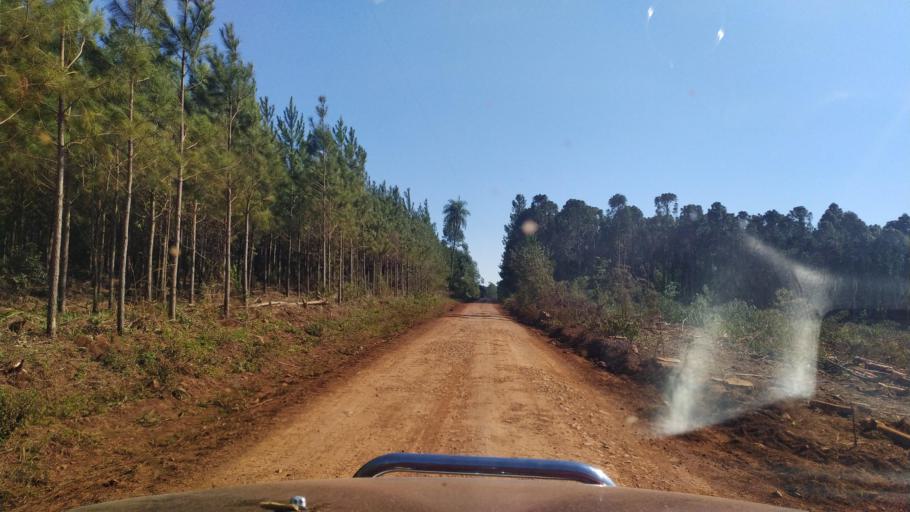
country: AR
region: Misiones
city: El Alcazar
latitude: -26.7342
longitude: -54.6675
